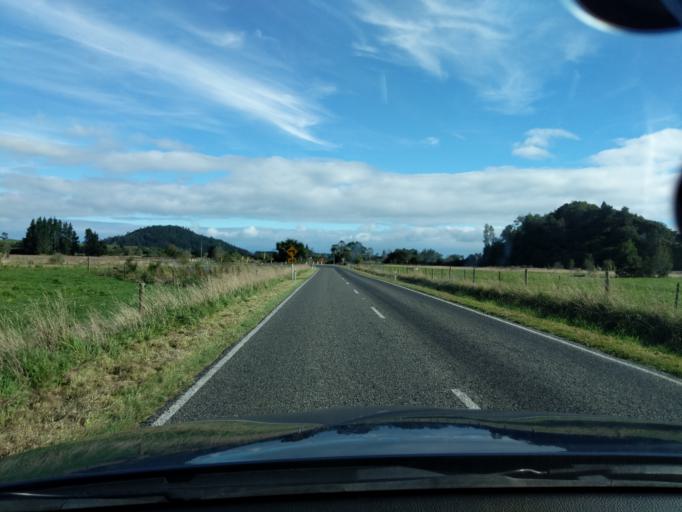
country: NZ
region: Tasman
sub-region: Tasman District
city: Takaka
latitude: -40.8478
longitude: 172.8394
